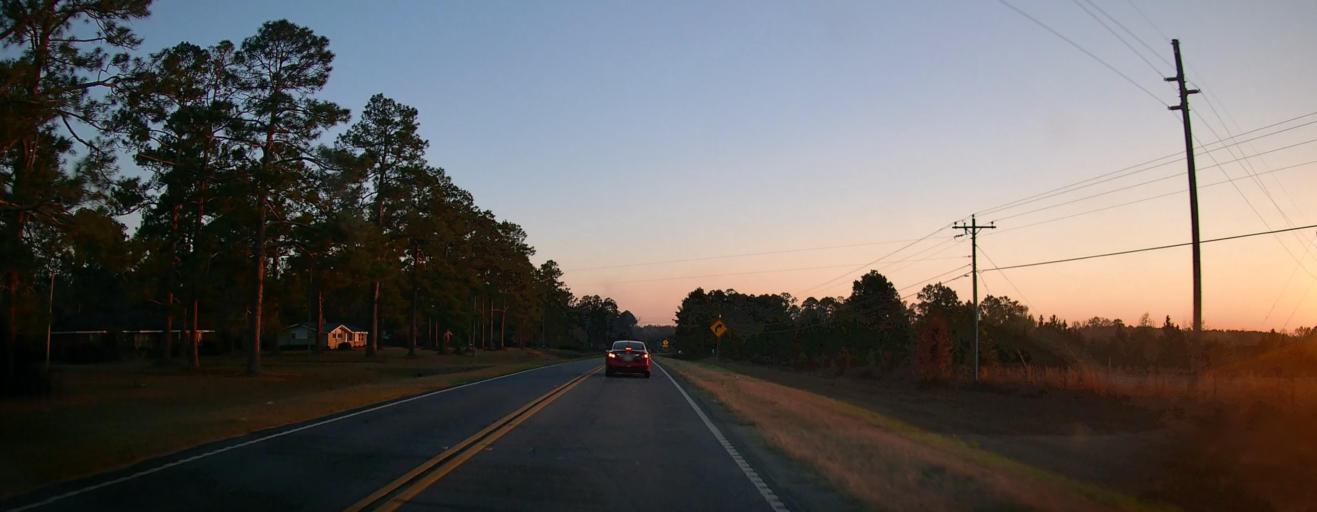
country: US
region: Georgia
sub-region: Dodge County
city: Eastman
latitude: 32.2127
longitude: -83.1607
